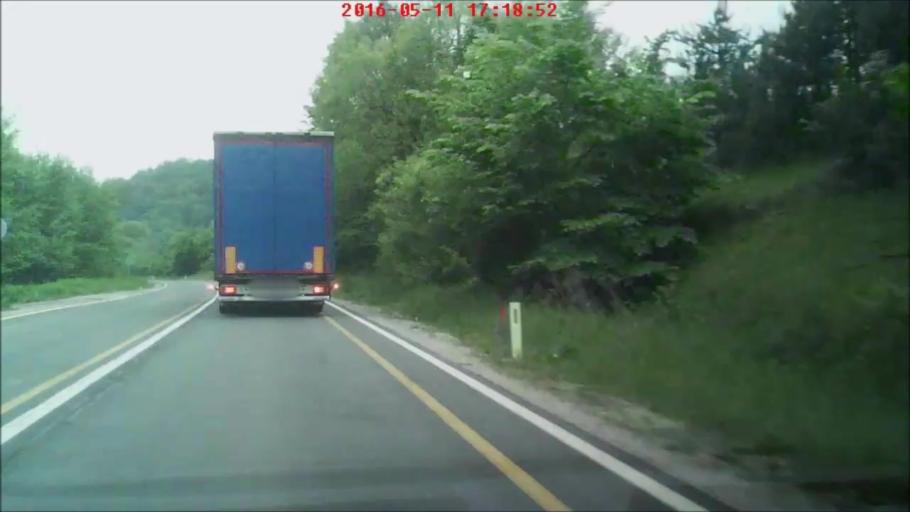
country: SI
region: Podlehnik
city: Podlehnik
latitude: 46.3033
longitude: 15.8581
